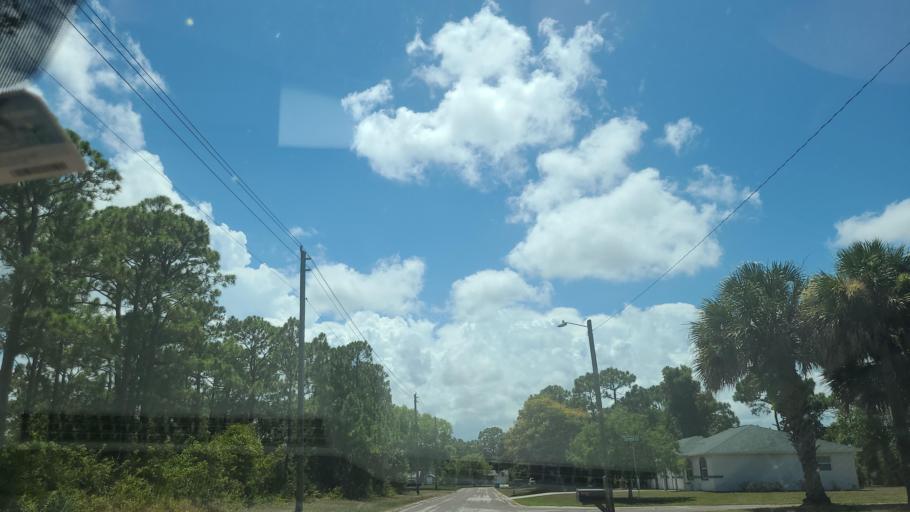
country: US
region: Florida
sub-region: Indian River County
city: Sebastian
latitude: 27.7728
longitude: -80.4676
